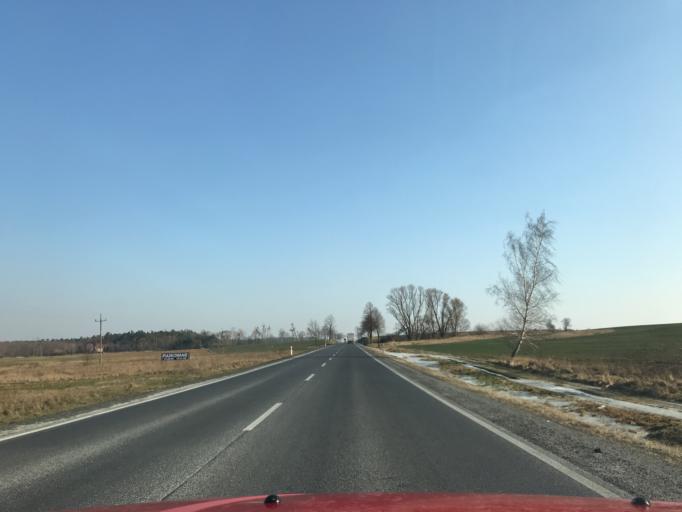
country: PL
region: Greater Poland Voivodeship
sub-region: Powiat sredzki
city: Nowe Miasto nad Warta
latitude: 52.0824
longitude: 17.4057
